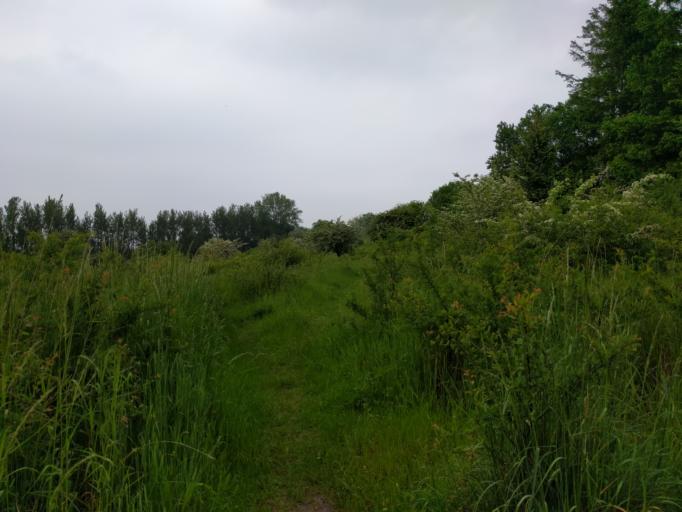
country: DK
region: South Denmark
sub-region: Kerteminde Kommune
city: Munkebo
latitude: 55.4628
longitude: 10.5509
